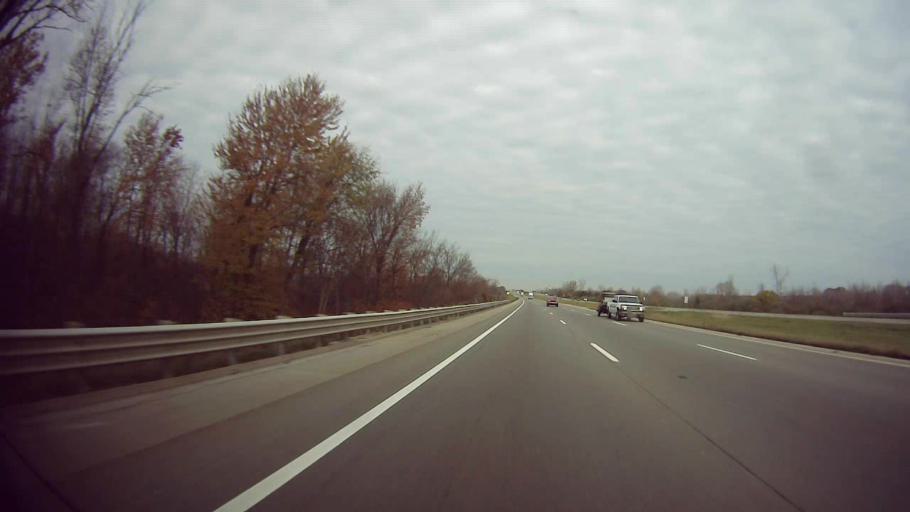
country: US
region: Michigan
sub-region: Monroe County
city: Carleton
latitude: 42.0733
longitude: -83.3680
